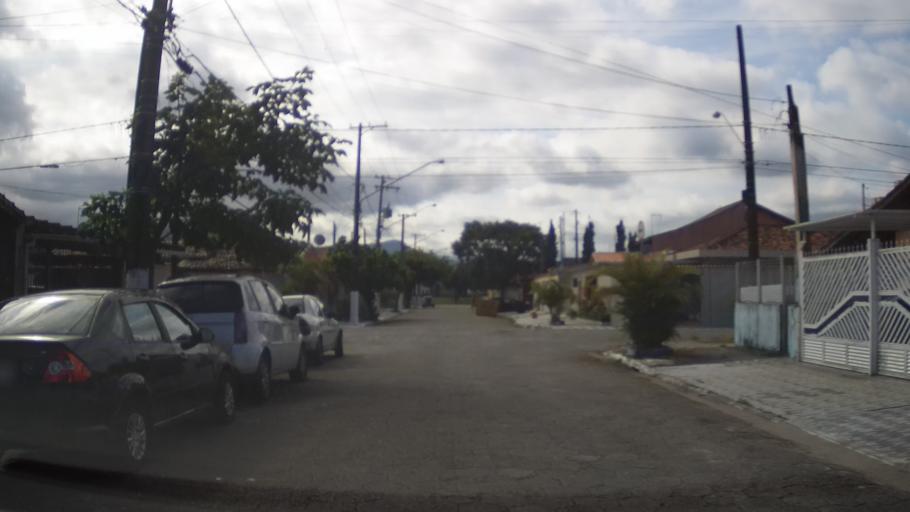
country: BR
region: Sao Paulo
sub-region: Praia Grande
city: Praia Grande
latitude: -24.0170
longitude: -46.4600
